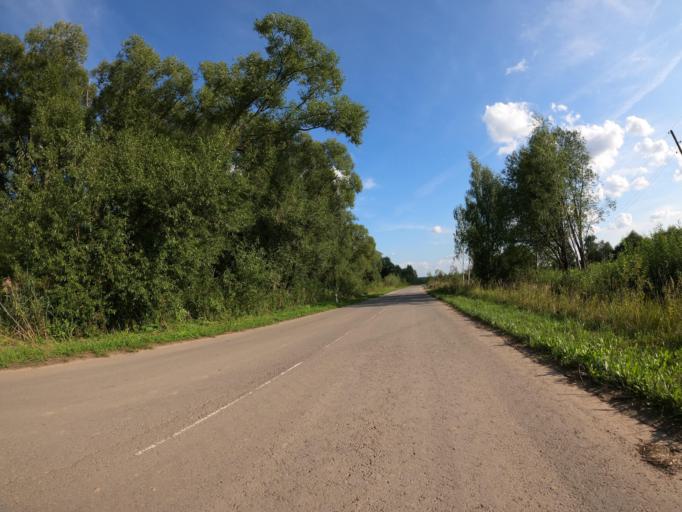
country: RU
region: Moskovskaya
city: Troitskoye
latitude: 55.2088
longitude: 38.4880
